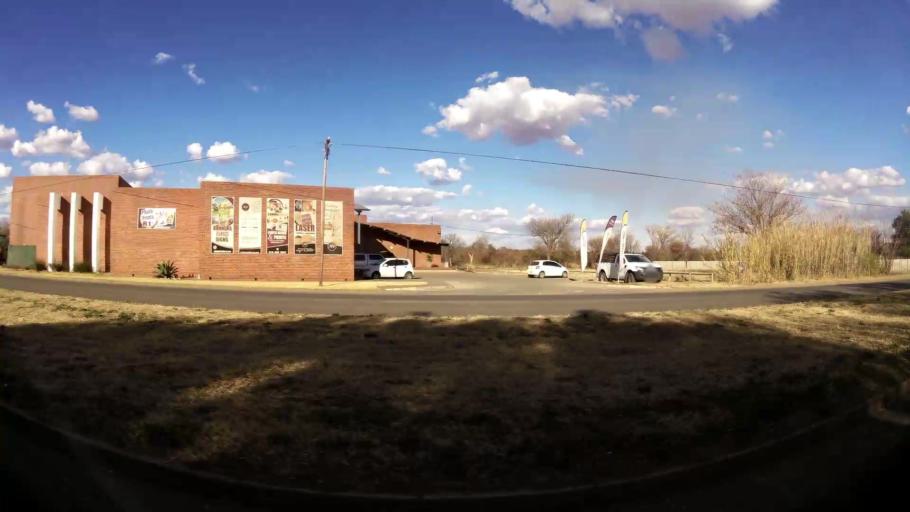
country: ZA
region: North-West
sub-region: Dr Kenneth Kaunda District Municipality
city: Klerksdorp
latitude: -26.8341
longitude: 26.6613
